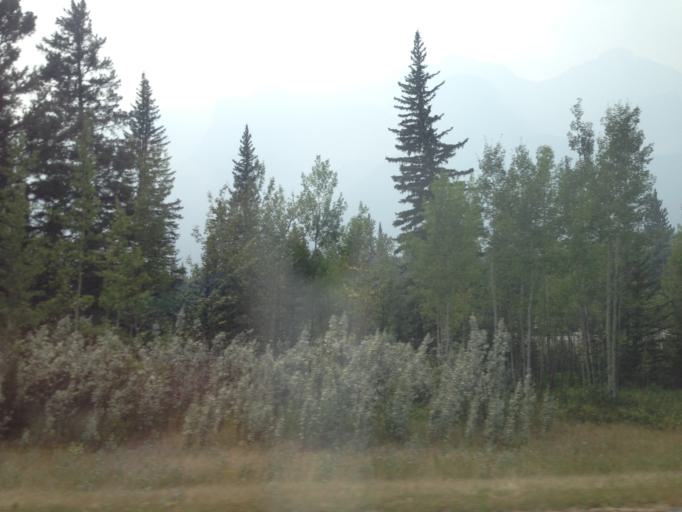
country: CA
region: Alberta
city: Canmore
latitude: 51.1476
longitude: -115.4248
